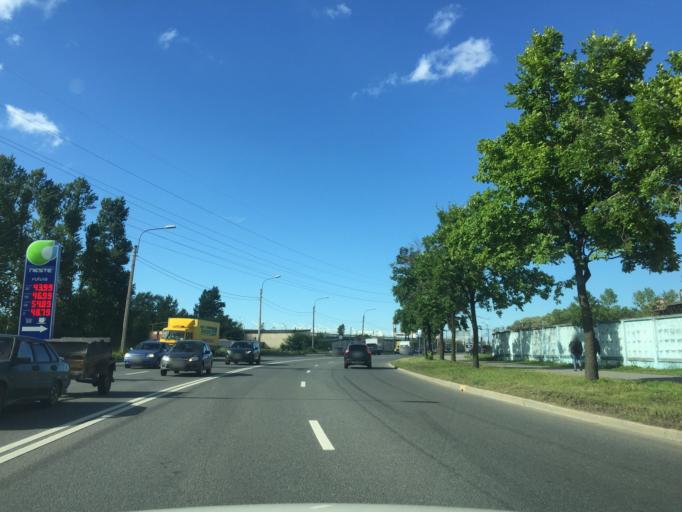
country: RU
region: St.-Petersburg
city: Avtovo
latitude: 59.8466
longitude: 30.2922
